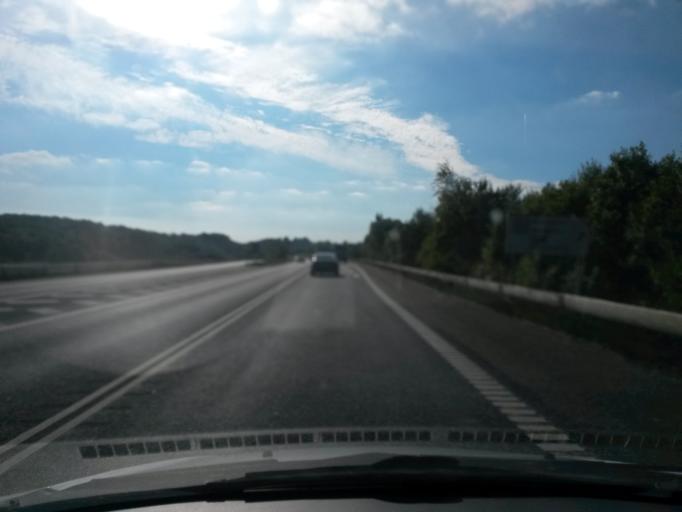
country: DK
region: Central Jutland
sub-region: Syddjurs Kommune
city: Hornslet
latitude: 56.2941
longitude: 10.3354
